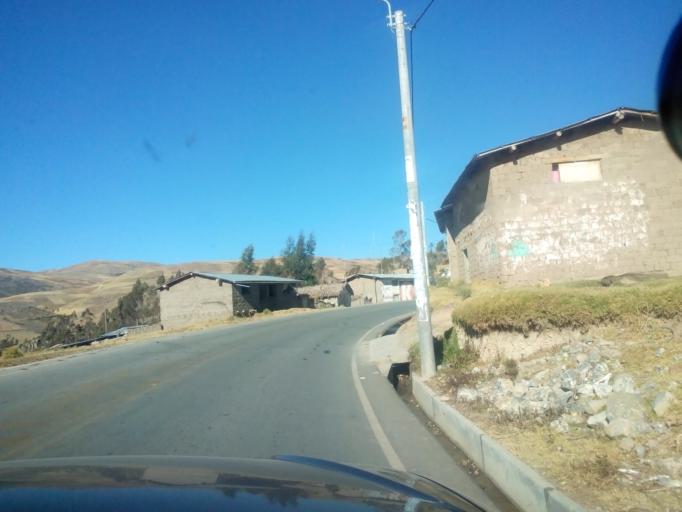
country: PE
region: Apurimac
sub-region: Provincia de Andahuaylas
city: Pacucha
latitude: -13.6501
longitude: -73.2978
